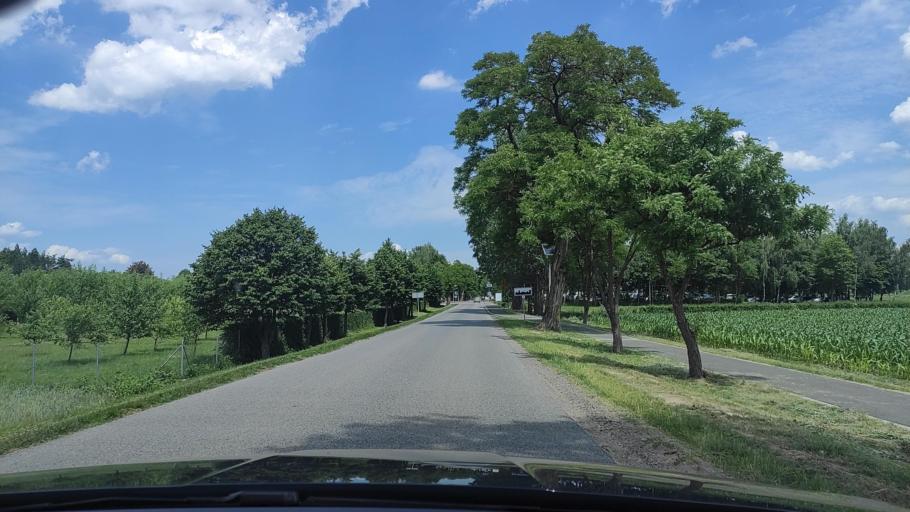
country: PL
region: Greater Poland Voivodeship
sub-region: Powiat gnieznienski
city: Lubowo
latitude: 52.5111
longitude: 17.3831
